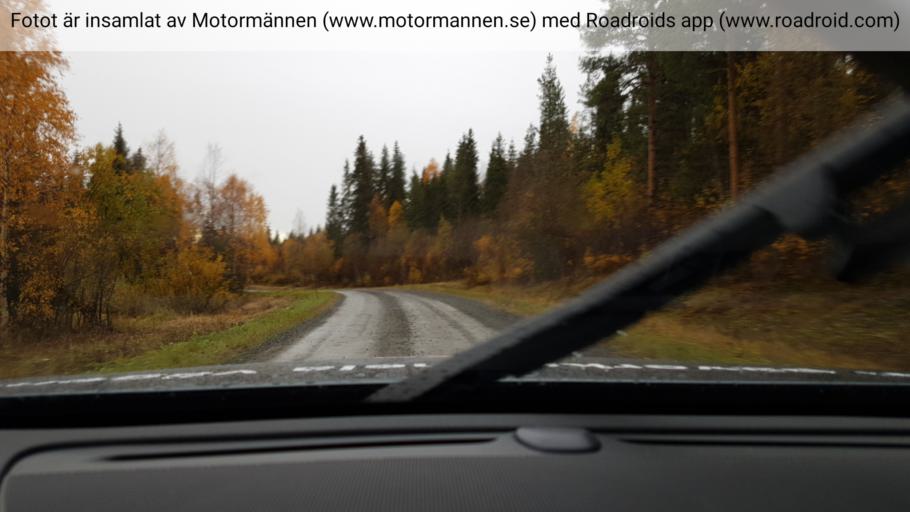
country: SE
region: Norrbotten
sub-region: Pajala Kommun
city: Pajala
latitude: 66.9646
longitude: 22.9376
